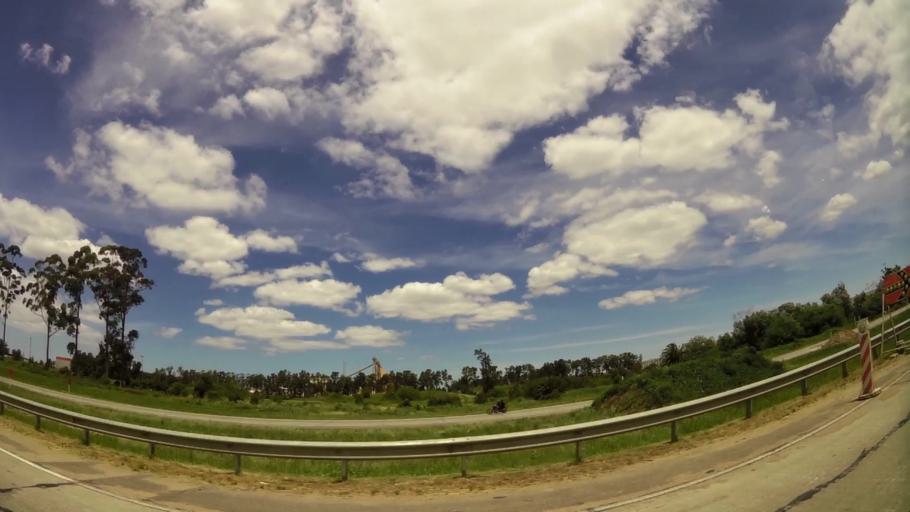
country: UY
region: Montevideo
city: Pajas Blancas
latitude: -34.8531
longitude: -56.2816
